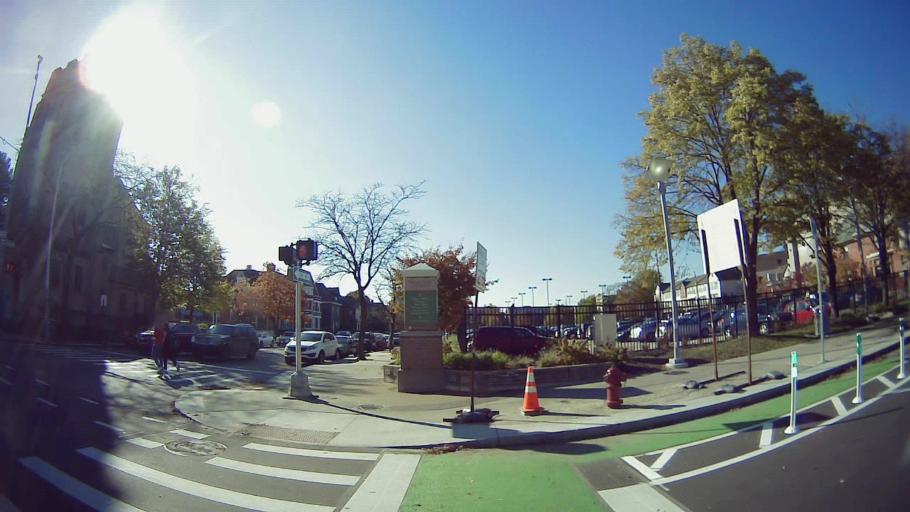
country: US
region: Michigan
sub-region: Wayne County
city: Detroit
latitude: 42.3538
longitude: -83.0654
